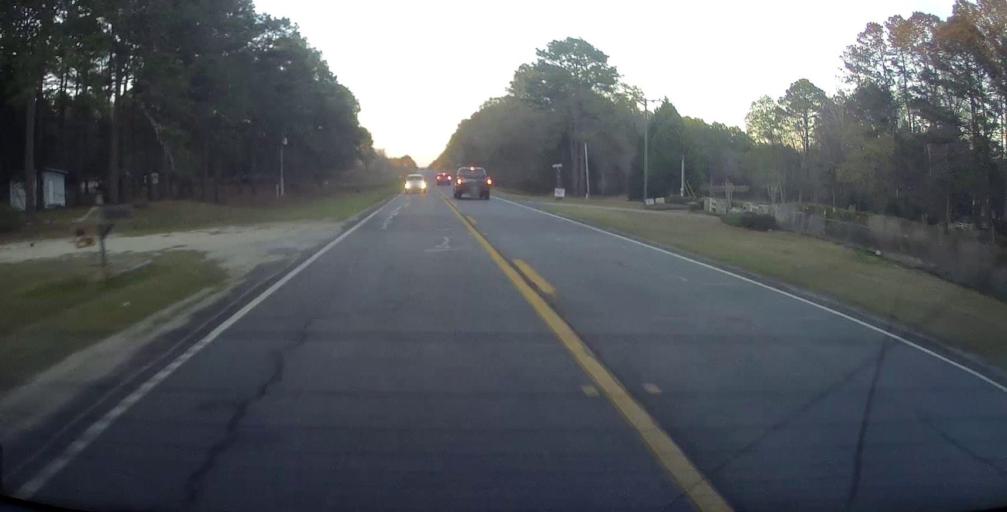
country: US
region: Georgia
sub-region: Dodge County
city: Eastman
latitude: 32.2197
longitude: -83.1572
